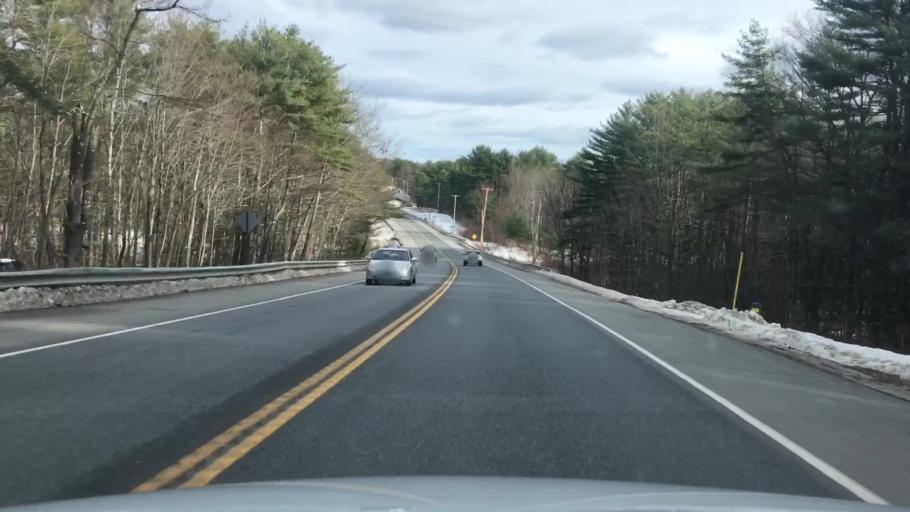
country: US
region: Maine
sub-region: Kennebec County
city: Monmouth
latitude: 44.2684
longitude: -70.0237
